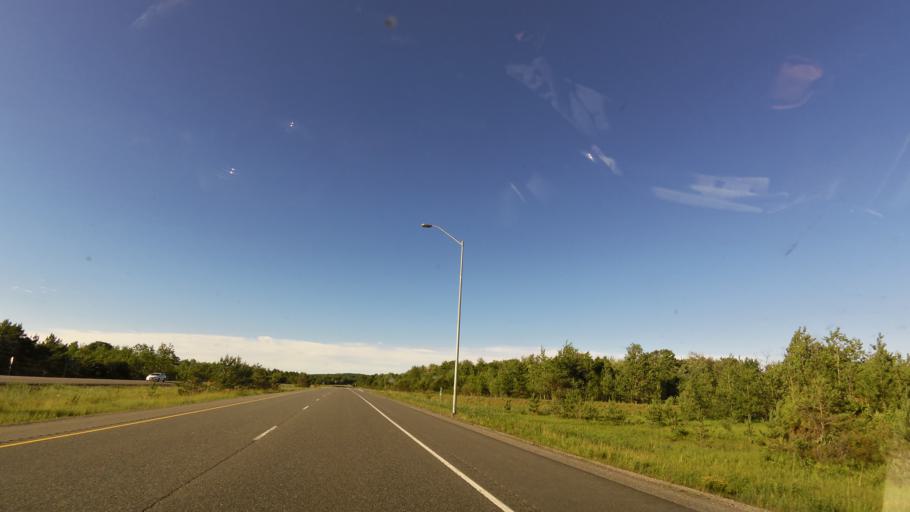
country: CA
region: Ontario
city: Barrie
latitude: 44.5529
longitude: -79.7447
